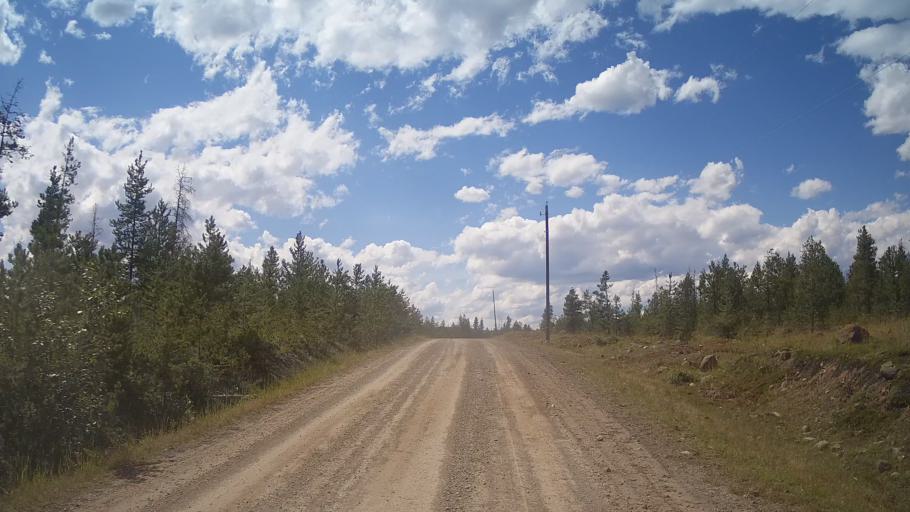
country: CA
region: British Columbia
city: Lillooet
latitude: 51.3358
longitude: -121.9656
